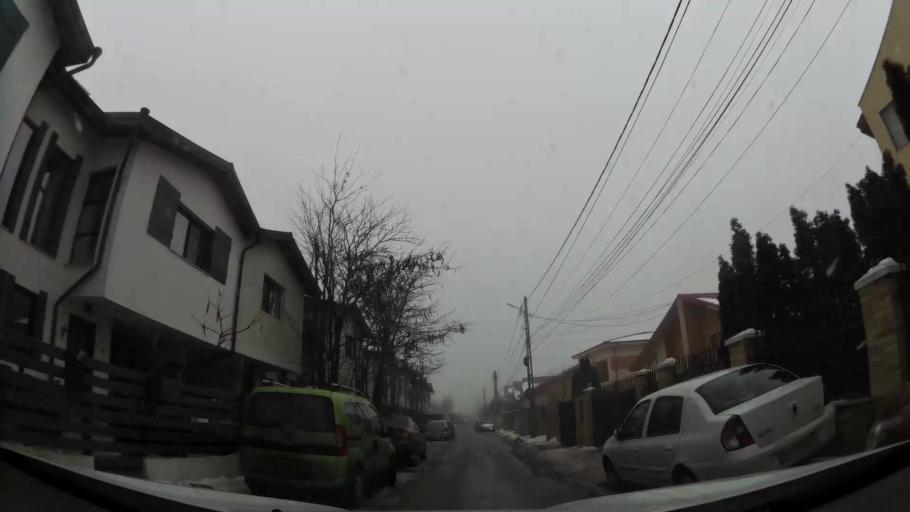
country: RO
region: Ilfov
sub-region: Comuna Chiajna
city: Rosu
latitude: 44.4524
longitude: 25.9925
